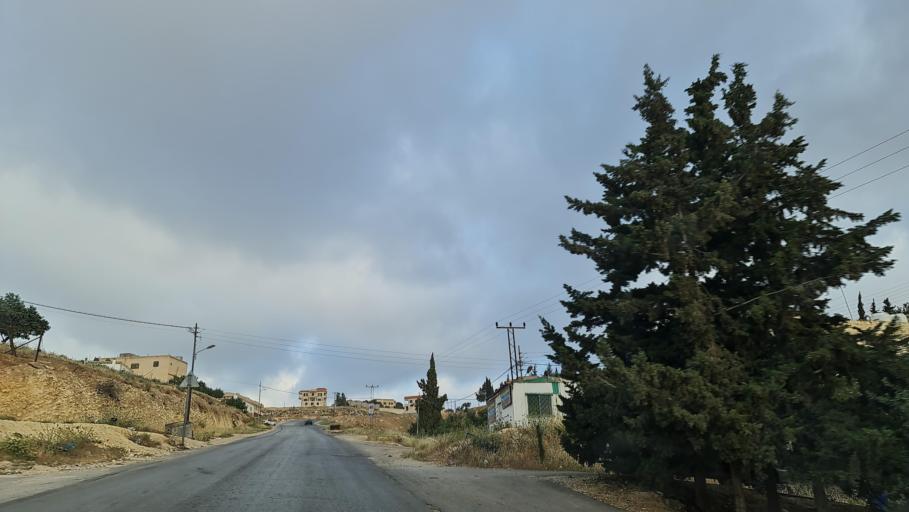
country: JO
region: Amman
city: Al Jubayhah
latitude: 32.0929
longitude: 35.9061
